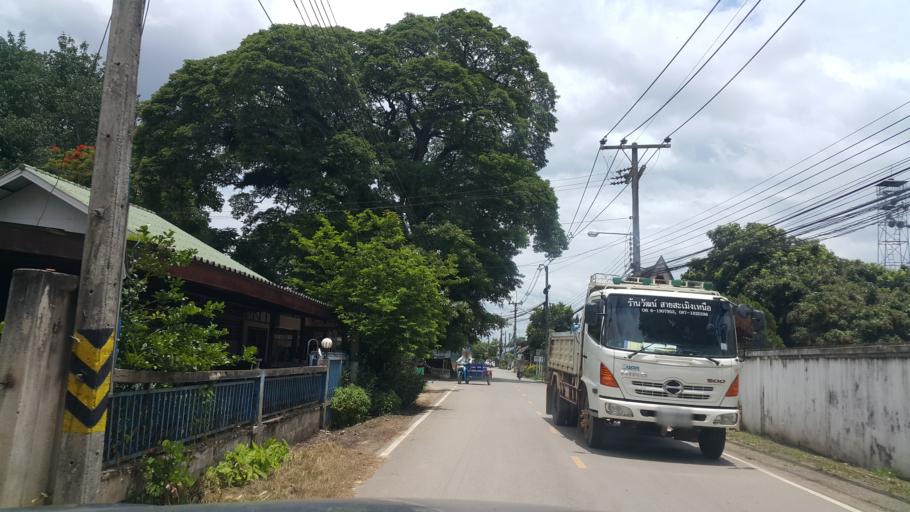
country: TH
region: Chiang Mai
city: Mae Taeng
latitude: 19.1860
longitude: 98.9901
